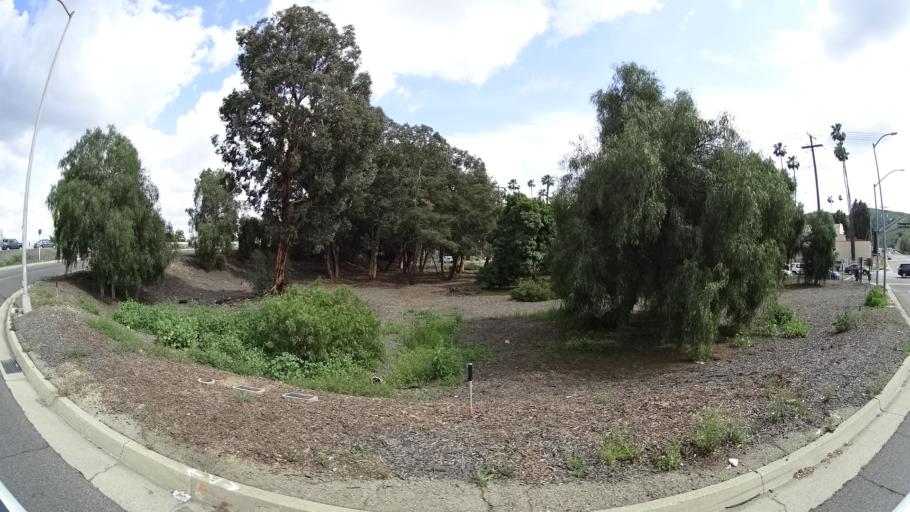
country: US
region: California
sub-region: Los Angeles County
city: Diamond Bar
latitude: 34.0619
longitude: -117.7914
